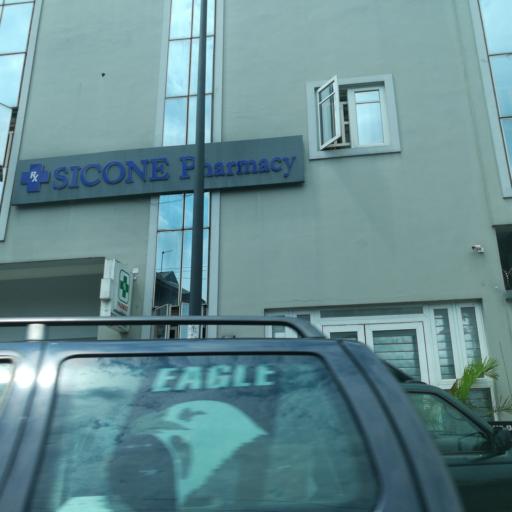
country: NG
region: Rivers
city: Port Harcourt
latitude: 4.8062
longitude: 7.0029
